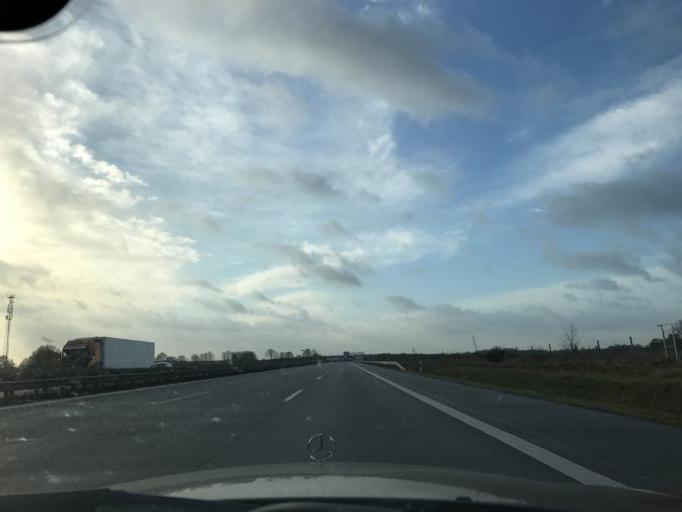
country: DE
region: Lower Saxony
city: Reessum
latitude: 53.1247
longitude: 9.2128
